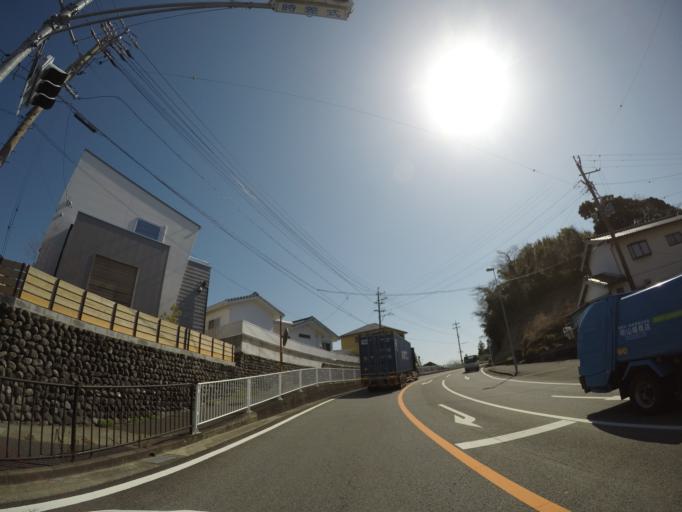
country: JP
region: Shizuoka
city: Kakegawa
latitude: 34.7610
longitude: 138.0805
